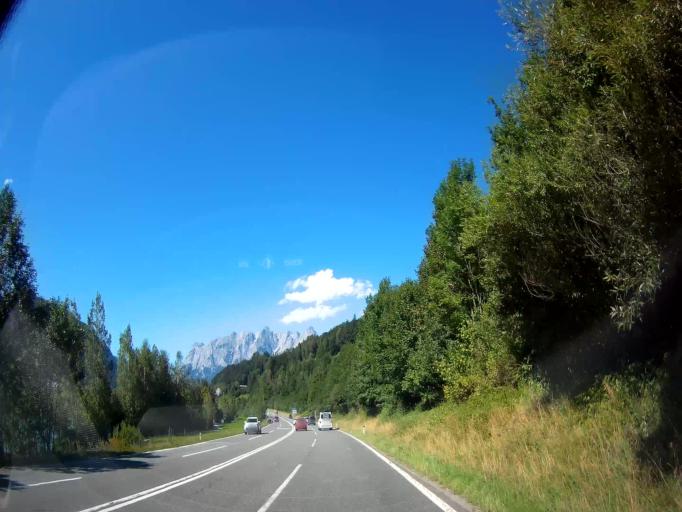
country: AT
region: Salzburg
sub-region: Politischer Bezirk Sankt Johann im Pongau
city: Bischofshofen
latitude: 47.3967
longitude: 13.2269
